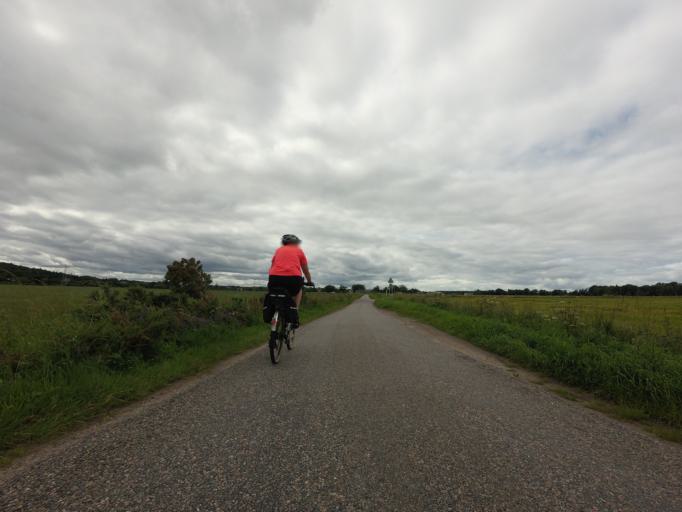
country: GB
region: Scotland
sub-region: Moray
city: Forres
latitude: 57.6246
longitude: -3.6074
